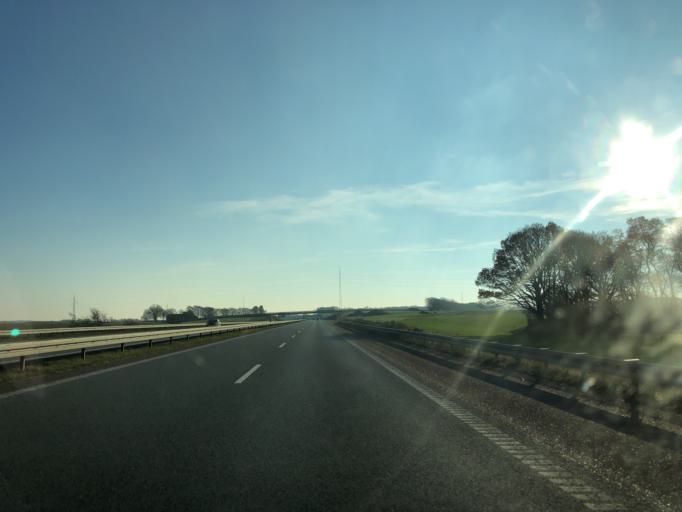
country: DK
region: South Denmark
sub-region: Vejle Kommune
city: Give
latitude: 55.8552
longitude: 9.2655
